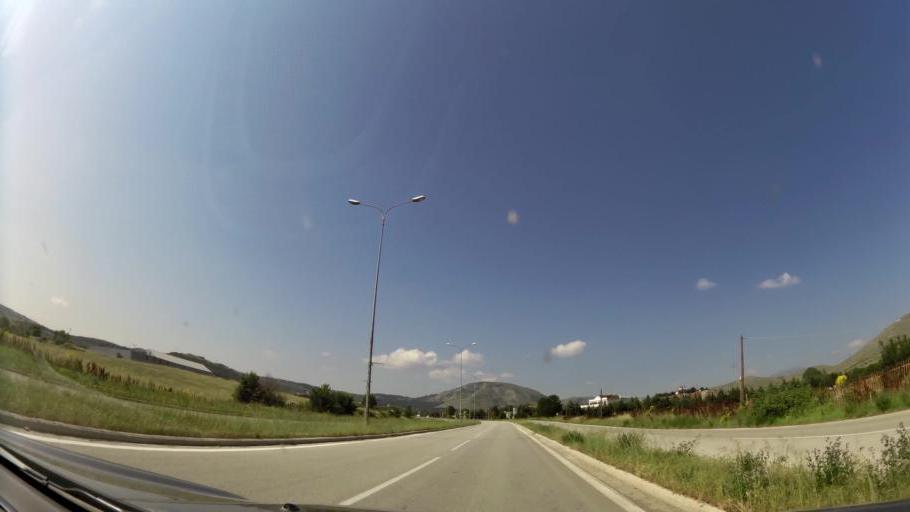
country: GR
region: West Macedonia
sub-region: Nomos Kozanis
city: Koila
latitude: 40.3414
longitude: 21.7949
